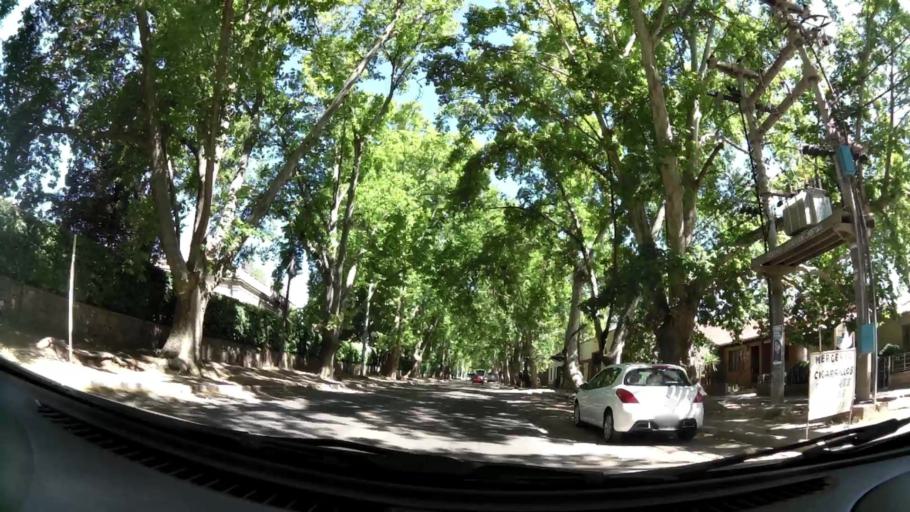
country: AR
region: Mendoza
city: Lujan de Cuyo
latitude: -32.9825
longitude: -68.8599
